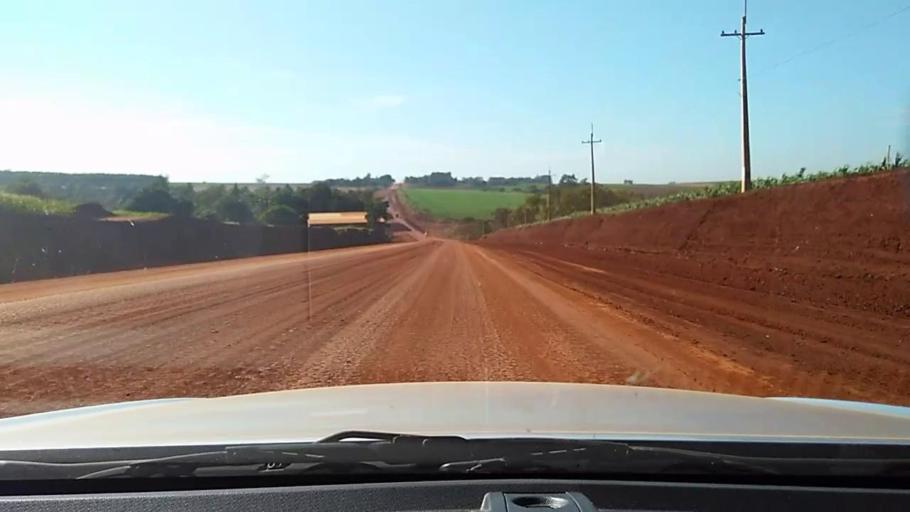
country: PY
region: Alto Parana
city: Naranjal
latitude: -25.9226
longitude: -55.4097
